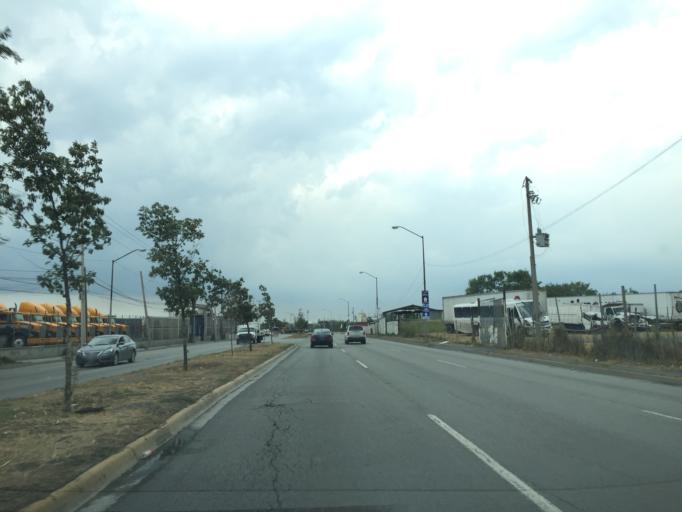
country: MX
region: Nuevo Leon
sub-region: Juarez
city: Valle de Juarez
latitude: 25.6715
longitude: -100.1697
